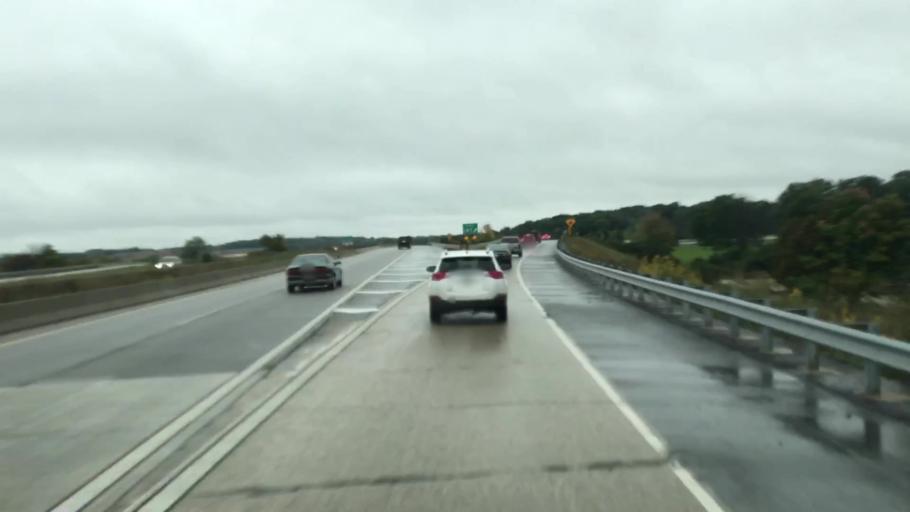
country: US
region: Wisconsin
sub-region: Waukesha County
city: Pewaukee
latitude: 43.0798
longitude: -88.2511
